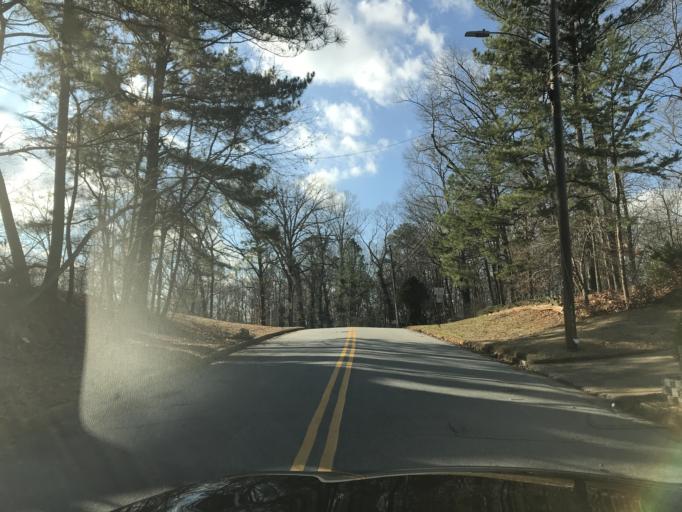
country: US
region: Georgia
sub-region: Fulton County
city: College Park
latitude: 33.6443
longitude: -84.4774
